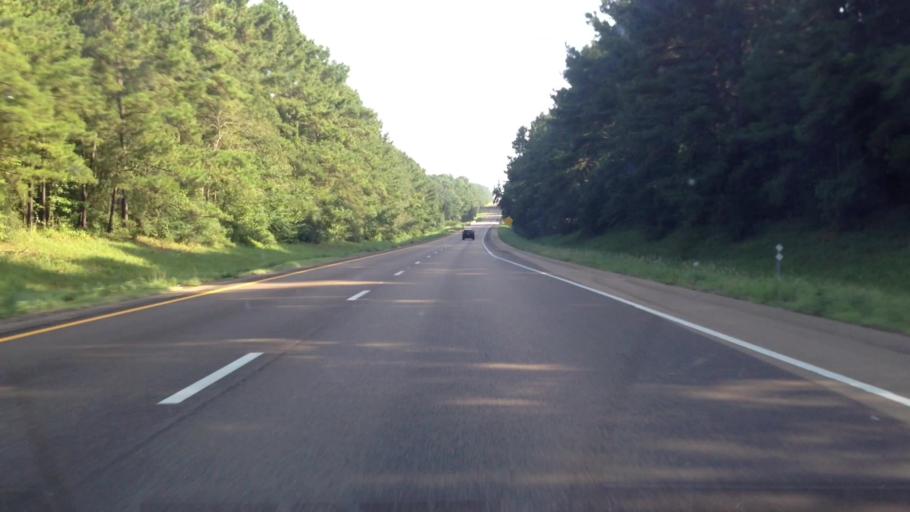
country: US
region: Mississippi
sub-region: Pike County
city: Summit
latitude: 31.3538
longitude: -90.4790
